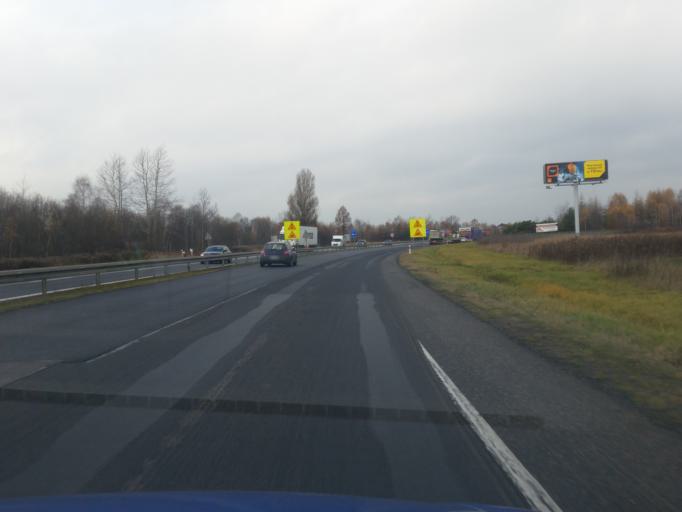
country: PL
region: Silesian Voivodeship
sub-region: Powiat myszkowski
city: Kozieglowy
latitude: 50.5936
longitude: 19.1525
